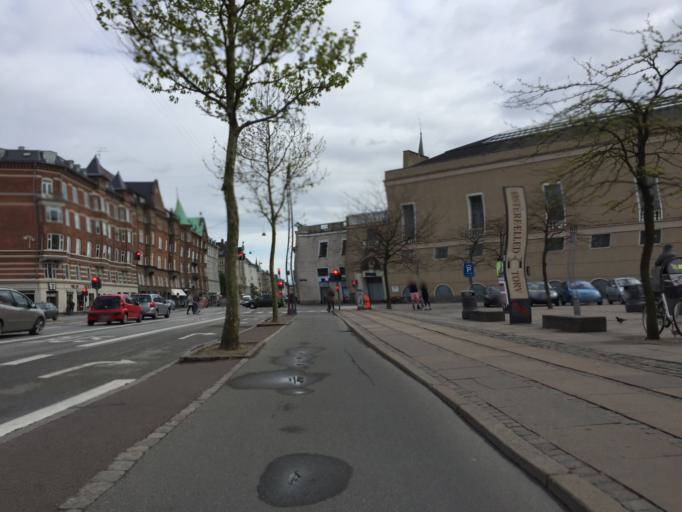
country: DK
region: Capital Region
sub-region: Kobenhavn
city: Copenhagen
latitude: 55.7051
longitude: 12.5772
